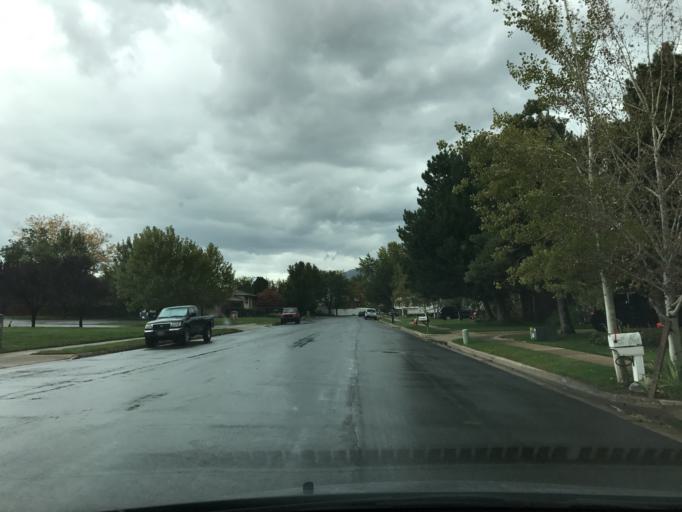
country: US
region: Utah
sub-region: Davis County
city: South Weber
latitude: 41.1087
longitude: -111.9156
